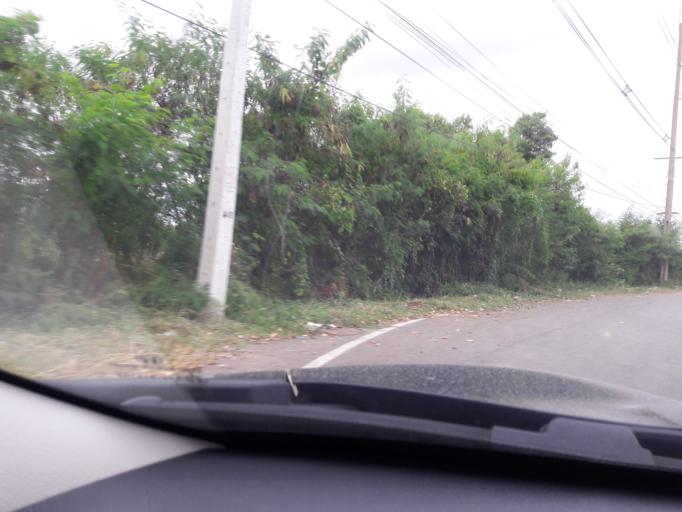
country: TH
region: Ratchaburi
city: Bang Phae
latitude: 13.6285
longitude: 99.9485
